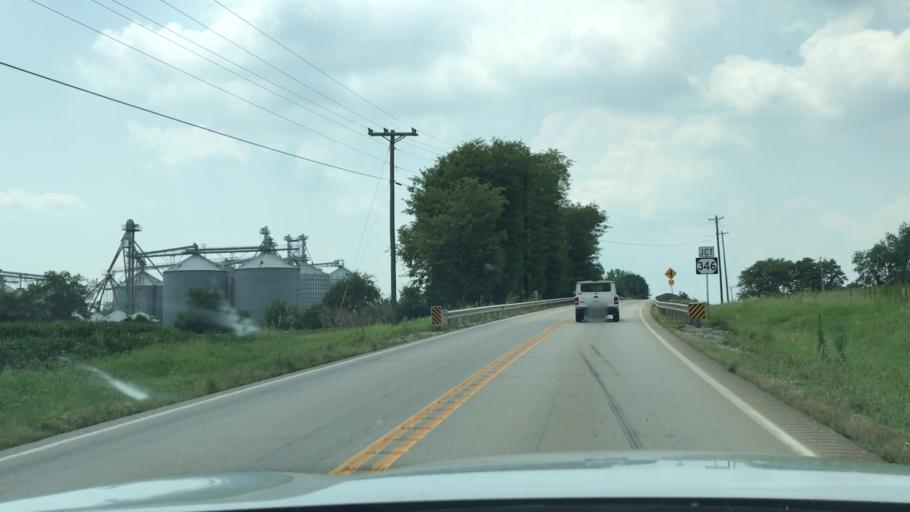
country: US
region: Kentucky
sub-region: Todd County
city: Guthrie
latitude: 36.6587
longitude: -87.1737
